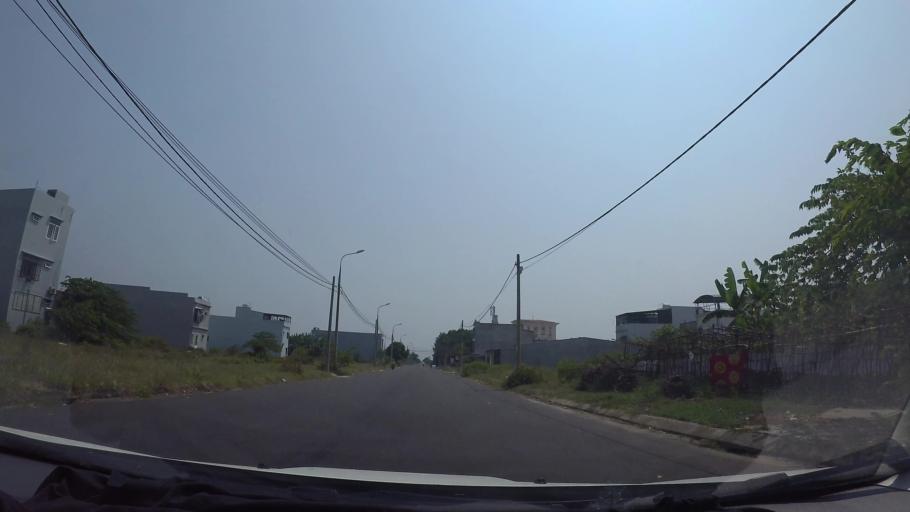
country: VN
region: Da Nang
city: Cam Le
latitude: 15.9840
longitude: 108.2114
